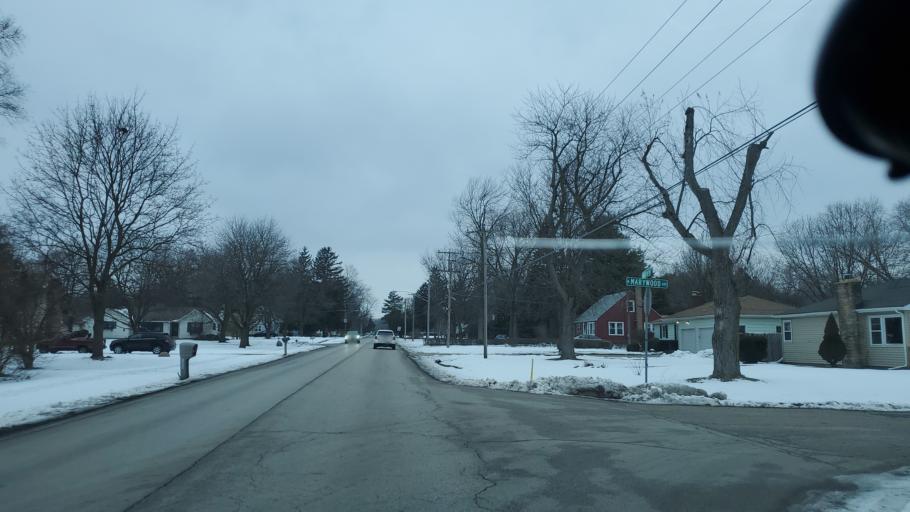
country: US
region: Illinois
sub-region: Kane County
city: North Aurora
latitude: 41.7937
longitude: -88.2851
